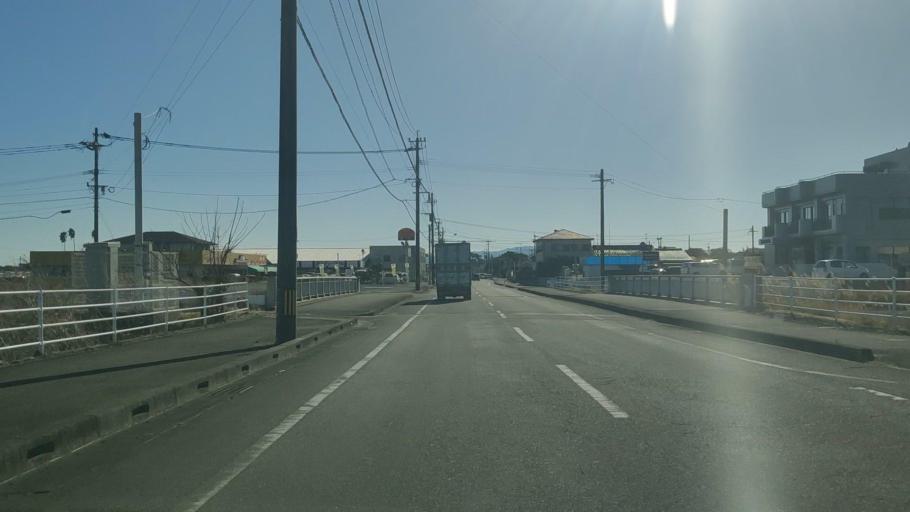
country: JP
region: Miyazaki
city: Miyazaki-shi
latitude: 31.9419
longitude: 131.4573
